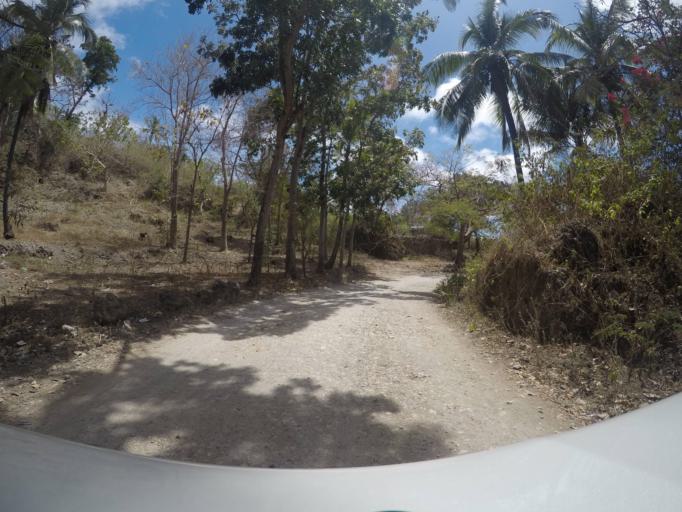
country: TL
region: Baucau
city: Baucau
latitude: -8.4558
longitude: 126.4428
